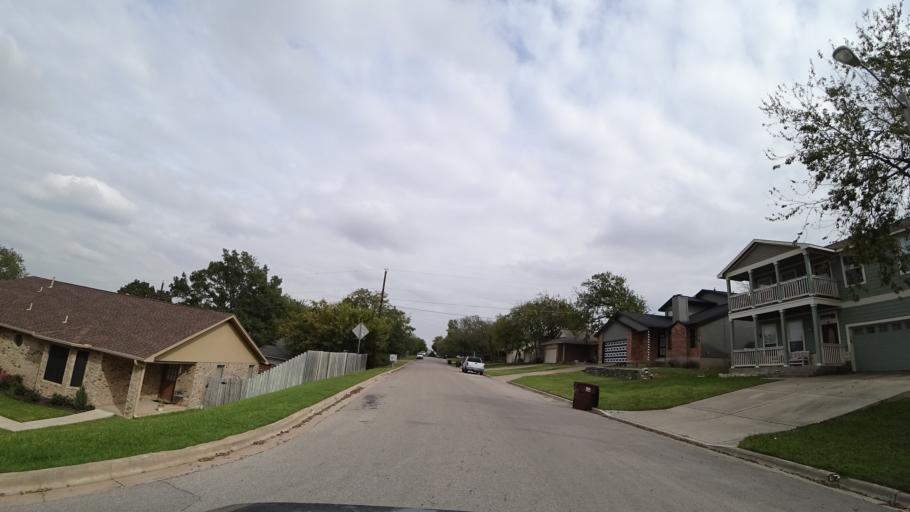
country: US
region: Texas
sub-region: Williamson County
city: Round Rock
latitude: 30.4864
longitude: -97.6873
